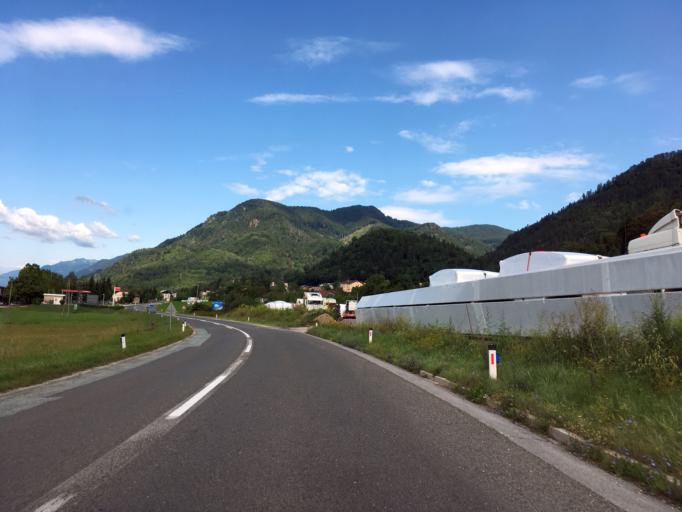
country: SI
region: Jesenice
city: Slovenski Javornik
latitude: 46.4218
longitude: 14.1054
